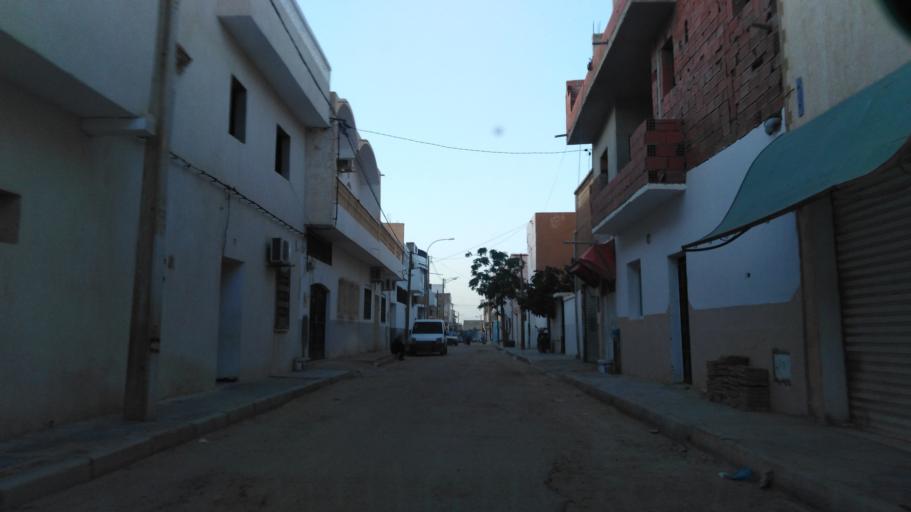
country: TN
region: Tataouine
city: Tataouine
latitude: 32.9345
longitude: 10.4529
